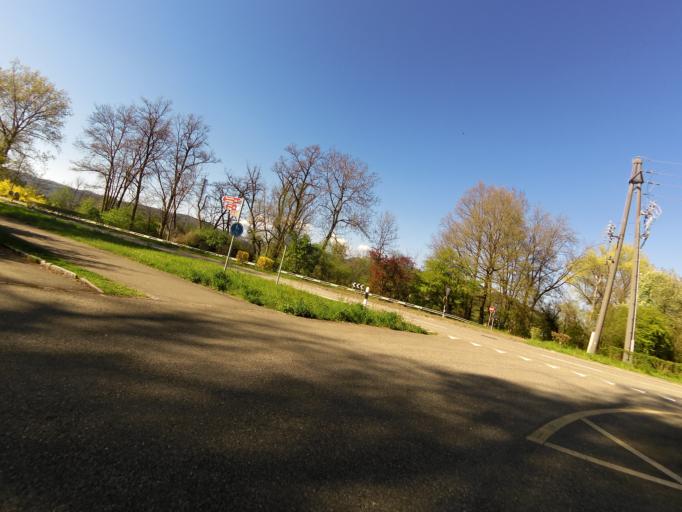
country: CH
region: Aargau
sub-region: Bezirk Zurzach
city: Koblenz
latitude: 47.6035
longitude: 8.2275
